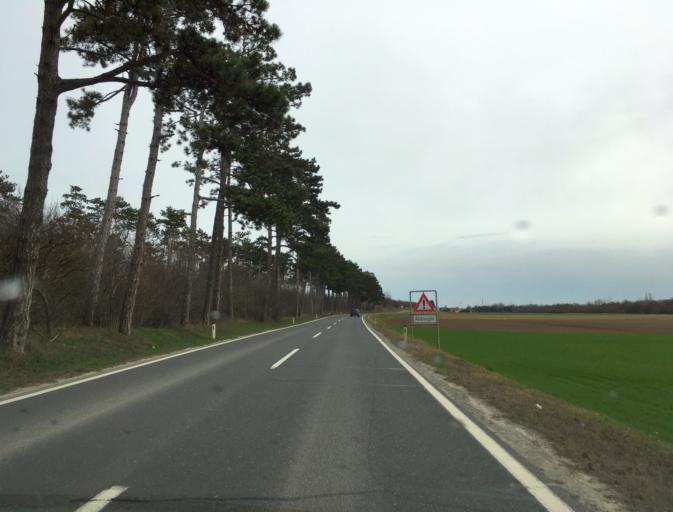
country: AT
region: Lower Austria
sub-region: Politischer Bezirk Ganserndorf
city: Deutsch-Wagram
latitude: 48.2871
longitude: 16.5724
